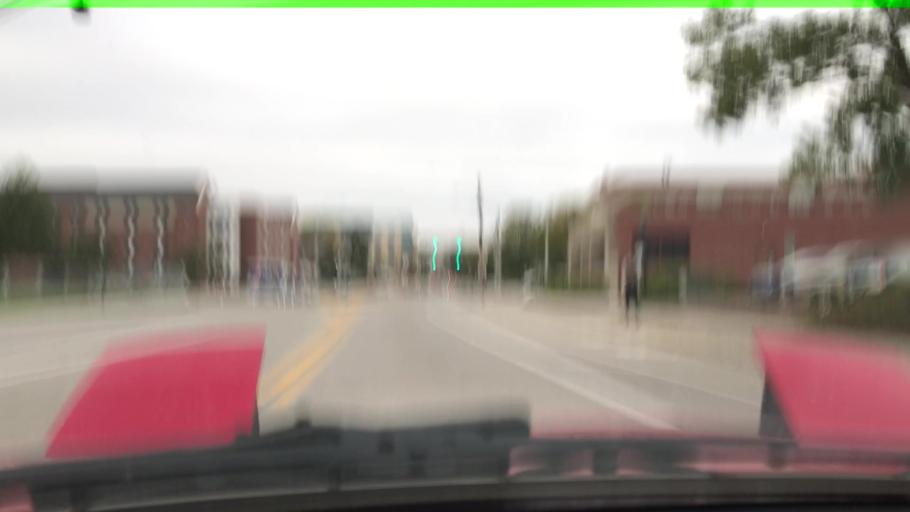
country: US
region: Nebraska
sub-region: Lancaster County
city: Lincoln
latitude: 40.8209
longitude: -96.6954
